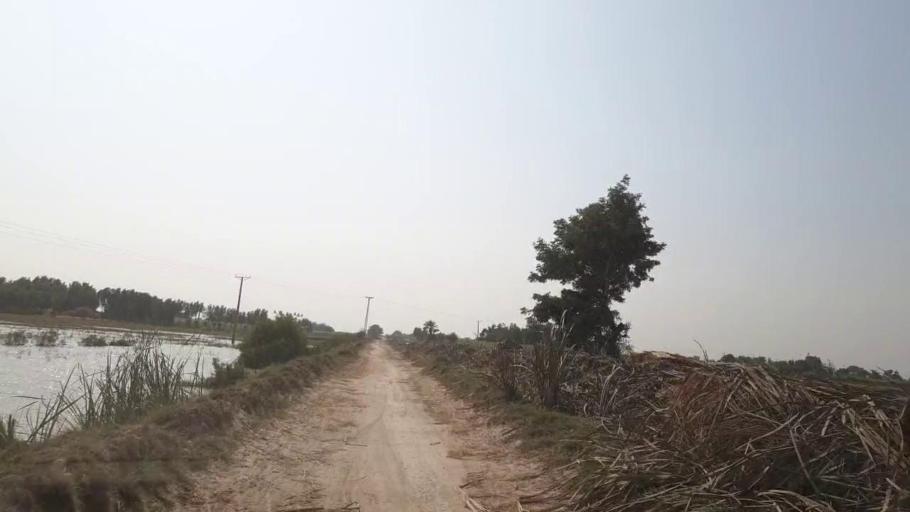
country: PK
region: Sindh
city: Bulri
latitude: 24.9620
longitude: 68.3904
